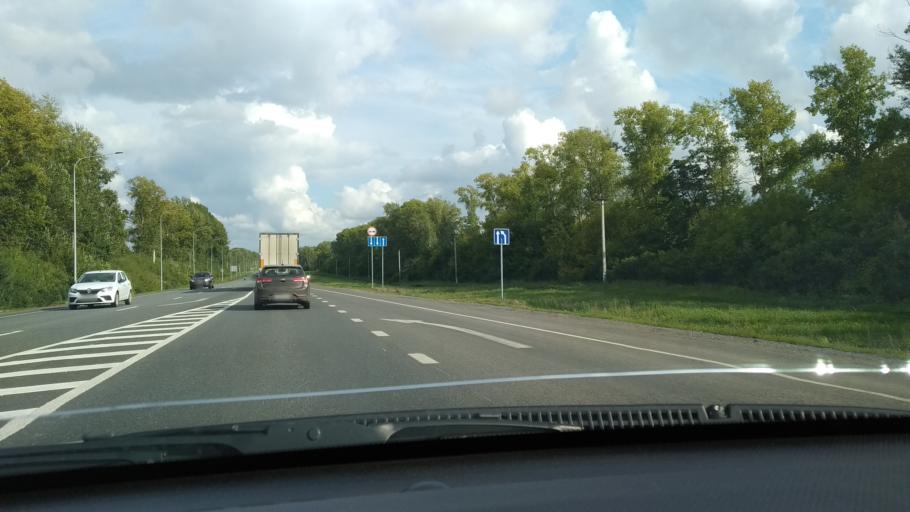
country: RU
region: Tatarstan
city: Stolbishchi
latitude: 55.6551
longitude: 49.3136
